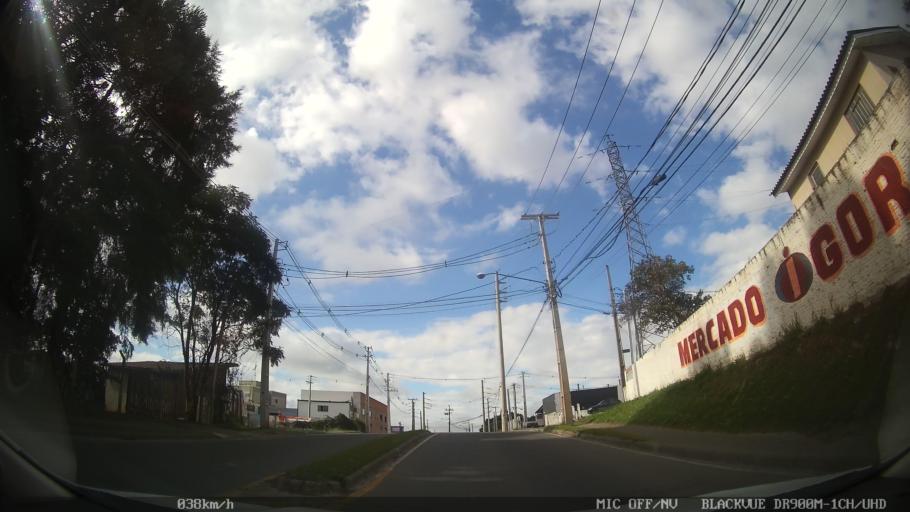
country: BR
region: Parana
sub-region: Colombo
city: Colombo
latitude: -25.3458
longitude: -49.1927
